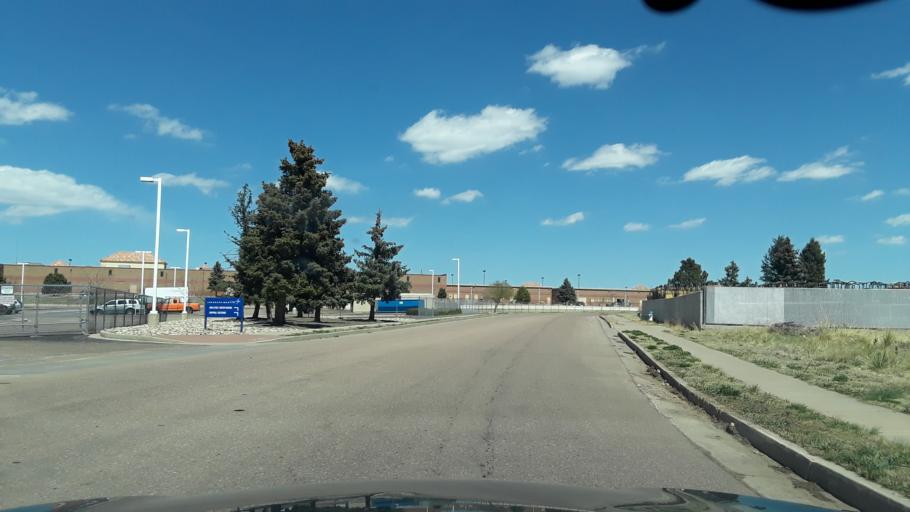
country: US
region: Colorado
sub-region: El Paso County
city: Cimarron Hills
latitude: 38.8677
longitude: -104.7184
